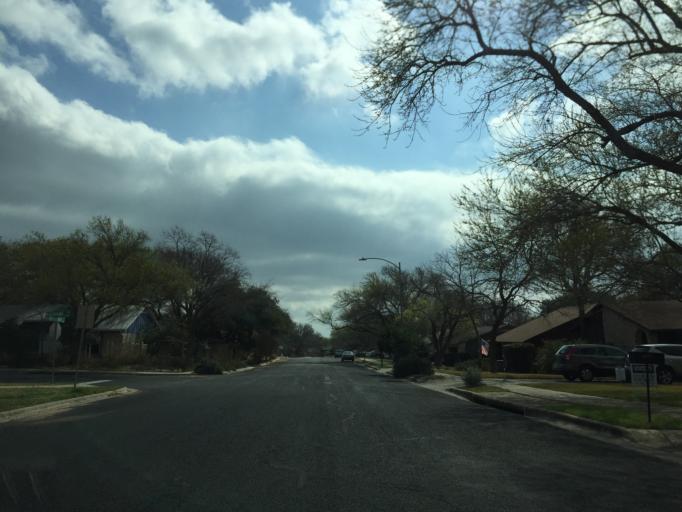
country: US
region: Texas
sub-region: Williamson County
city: Jollyville
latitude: 30.4121
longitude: -97.7379
